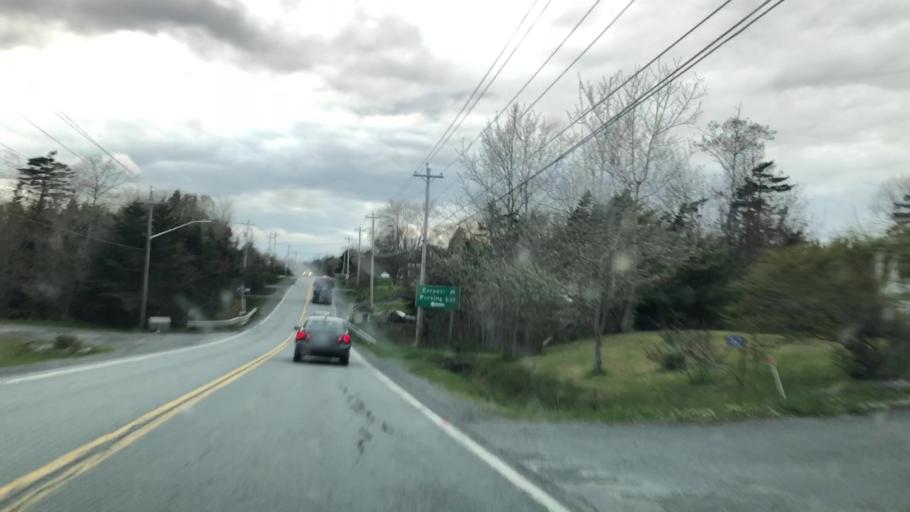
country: CA
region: Nova Scotia
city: Cole Harbour
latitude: 44.7838
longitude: -63.1638
